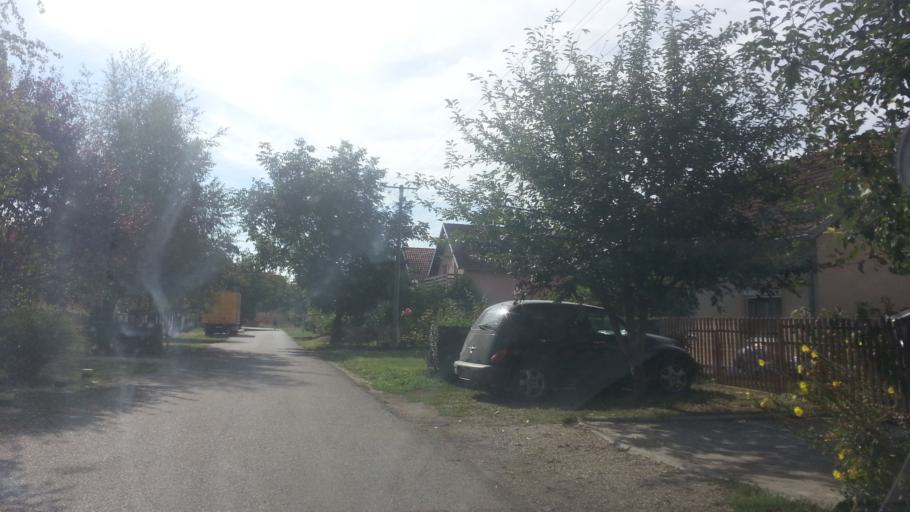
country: RS
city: Novi Banovci
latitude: 44.9685
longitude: 20.2754
